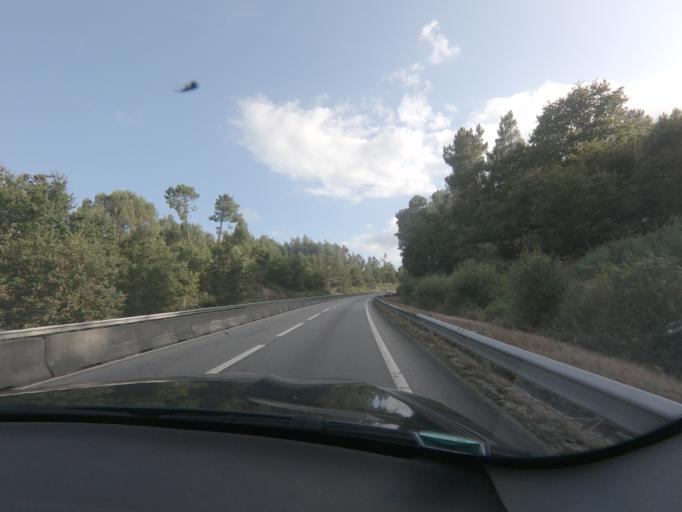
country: PT
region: Viseu
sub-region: Viseu
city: Viseu
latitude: 40.5980
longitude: -7.9968
